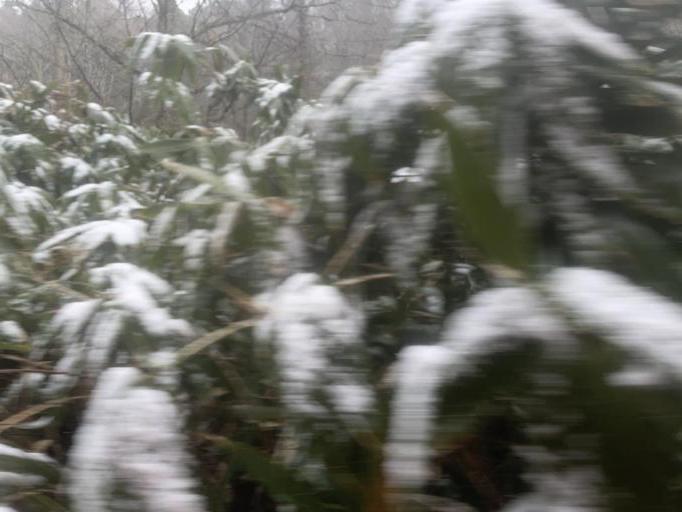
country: JP
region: Aomori
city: Goshogawara
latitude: 41.1007
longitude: 140.5281
